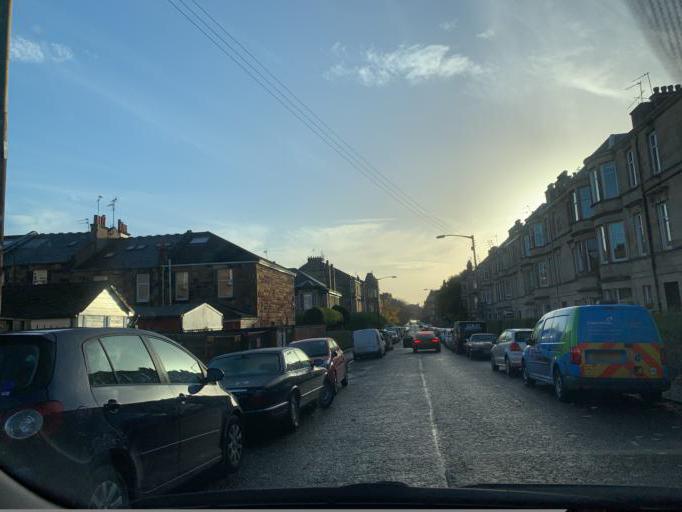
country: GB
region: Scotland
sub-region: East Renfrewshire
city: Giffnock
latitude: 55.8255
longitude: -4.2702
